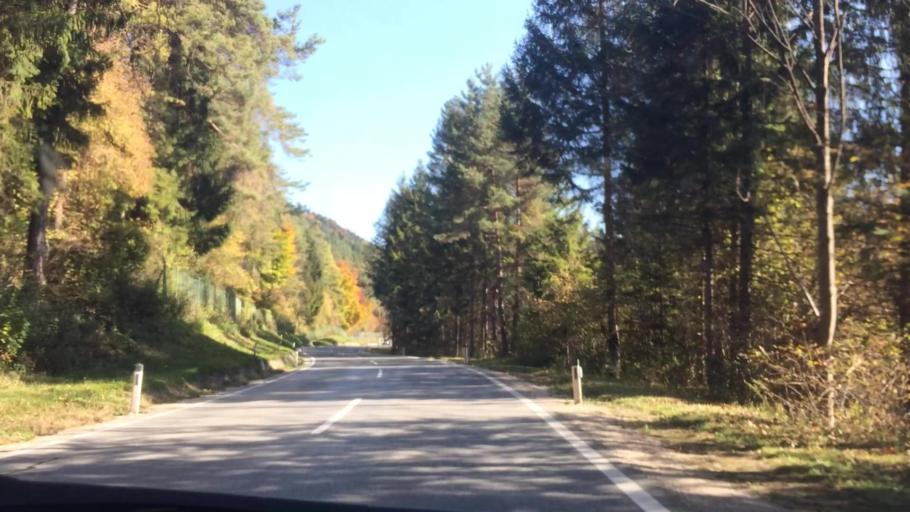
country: AT
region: Tyrol
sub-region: Politischer Bezirk Innsbruck Land
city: Vols
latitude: 47.2677
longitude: 11.3180
